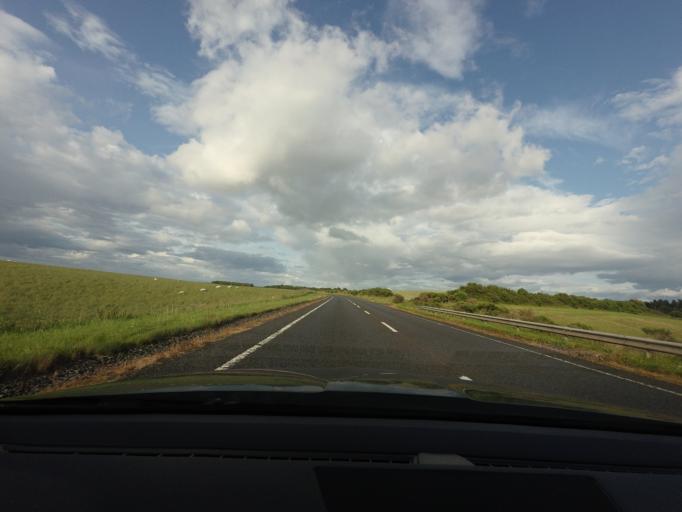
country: GB
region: Scotland
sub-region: Highland
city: Fortrose
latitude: 57.5350
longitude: -4.0314
